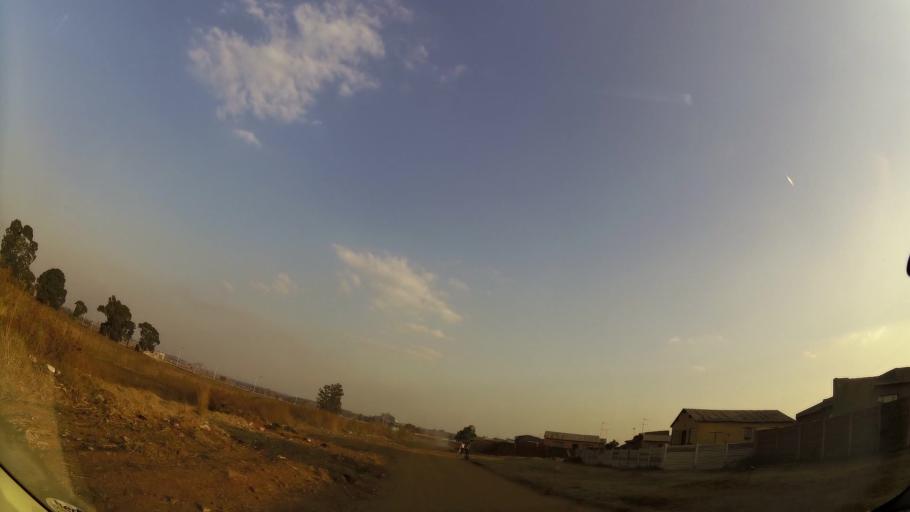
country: ZA
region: Gauteng
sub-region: Ekurhuleni Metropolitan Municipality
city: Benoni
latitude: -26.1623
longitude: 28.3825
